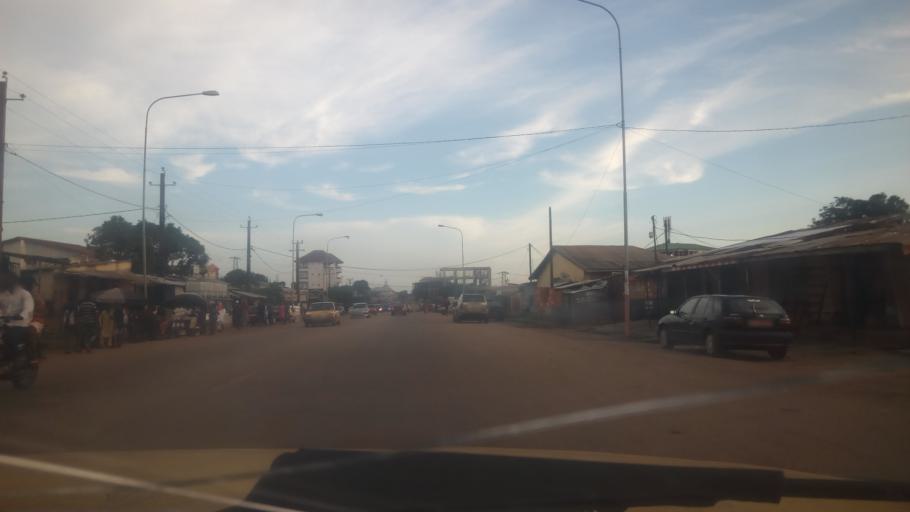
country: GN
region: Conakry
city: Conakry
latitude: 9.5741
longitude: -13.6529
